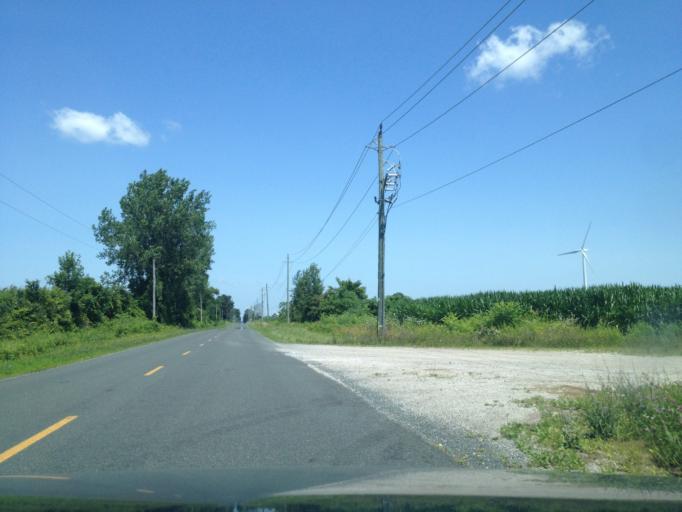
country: CA
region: Ontario
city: Aylmer
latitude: 42.6287
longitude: -80.7209
